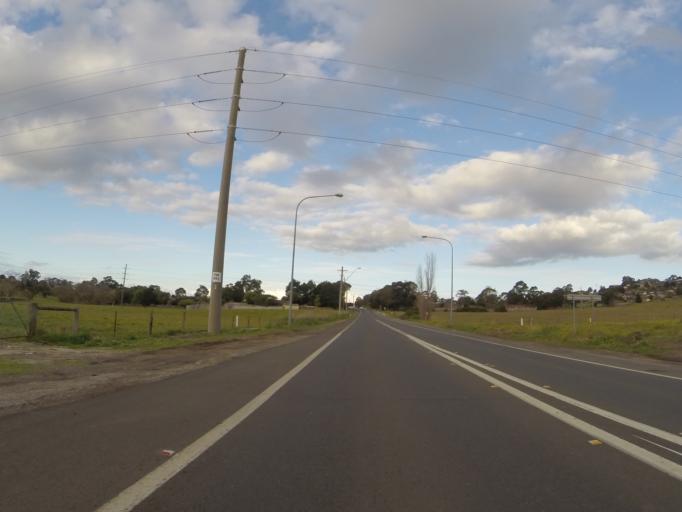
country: AU
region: New South Wales
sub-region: Shellharbour
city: Albion Park Rail
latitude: -34.5722
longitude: 150.7560
